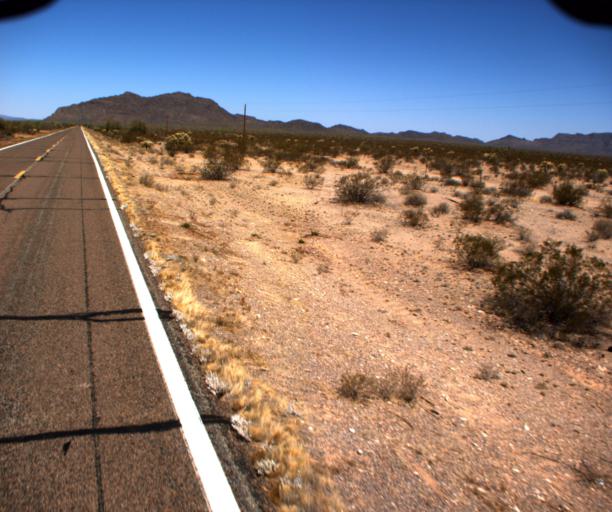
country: US
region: Arizona
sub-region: Pima County
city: Ajo
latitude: 32.2167
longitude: -112.6458
